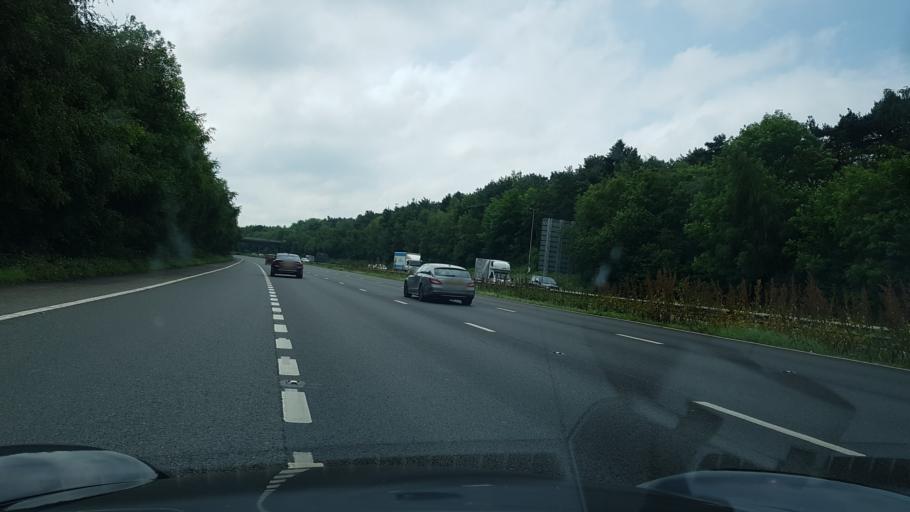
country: GB
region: England
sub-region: West Sussex
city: Maidenbower
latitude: 51.1285
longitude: -0.1417
